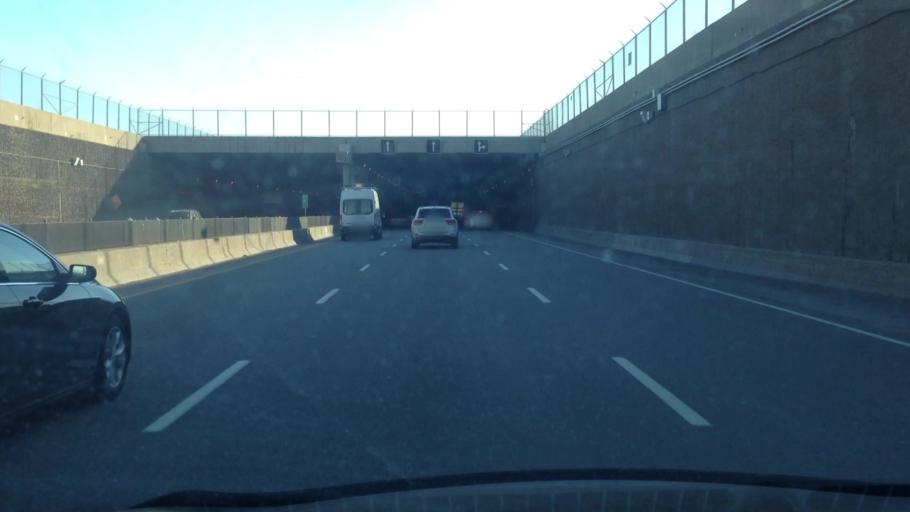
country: CA
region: Quebec
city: Dorval
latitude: 45.4800
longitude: -73.7187
